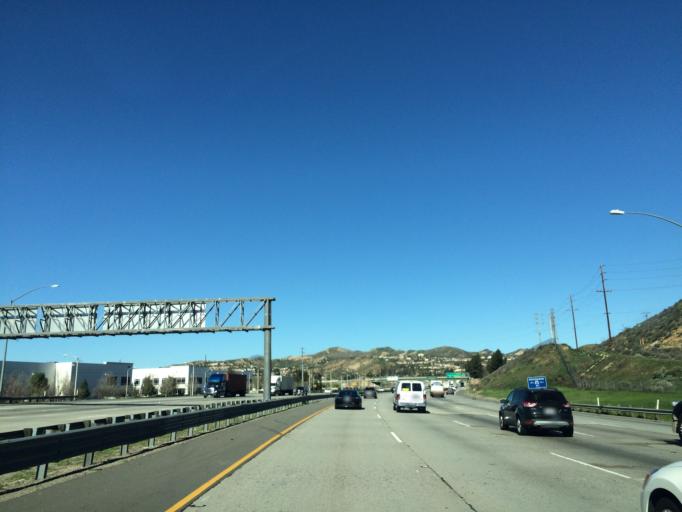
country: US
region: California
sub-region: Los Angeles County
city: Valencia
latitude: 34.4458
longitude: -118.6099
